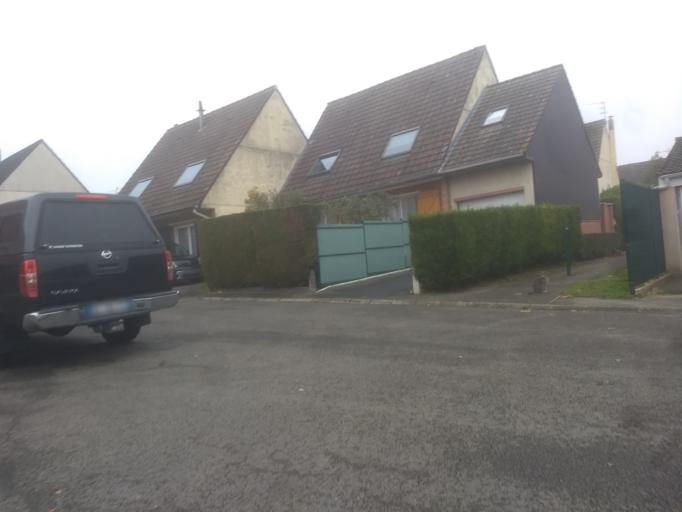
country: FR
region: Nord-Pas-de-Calais
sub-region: Departement du Pas-de-Calais
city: Saint-Nicolas
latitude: 50.3025
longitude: 2.7898
